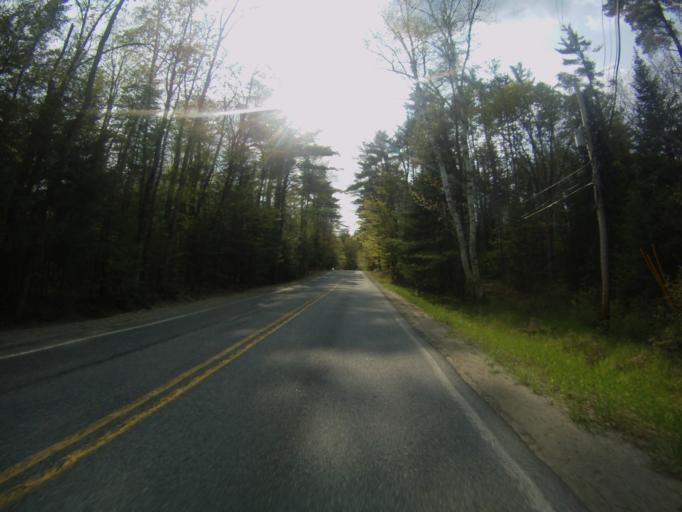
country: US
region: New York
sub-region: Warren County
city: Warrensburg
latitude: 43.8458
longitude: -73.8103
